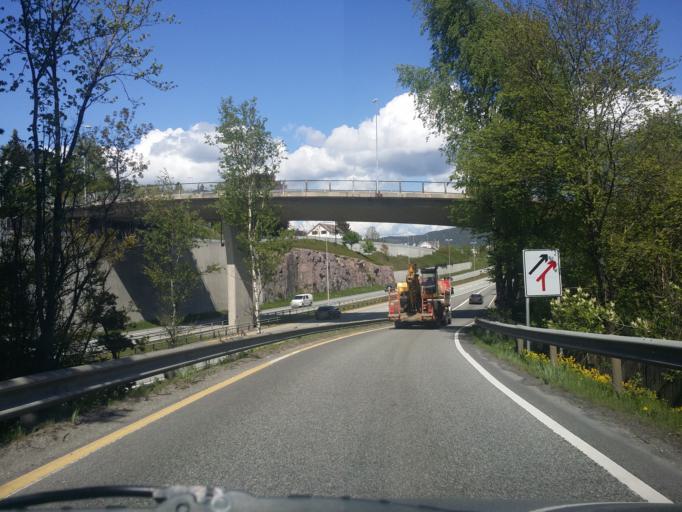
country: NO
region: Buskerud
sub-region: Drammen
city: Drammen
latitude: 59.7462
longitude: 10.2363
